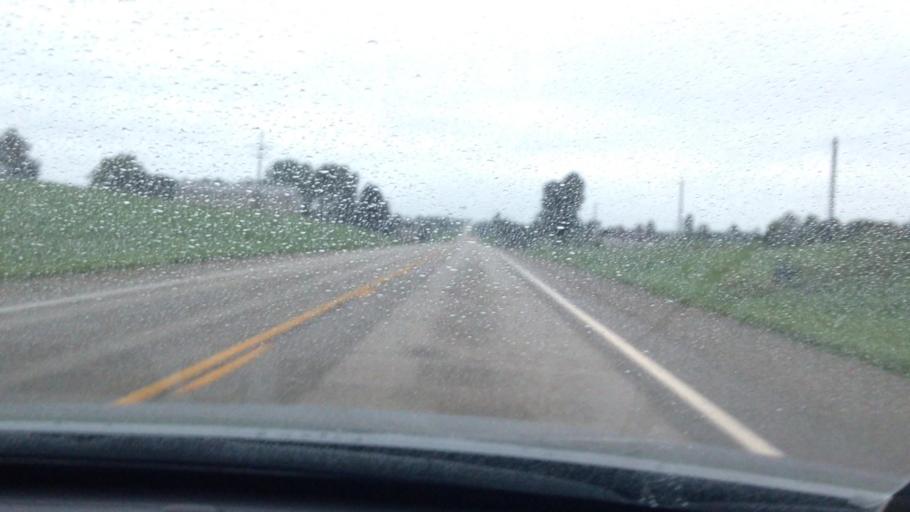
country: US
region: Kansas
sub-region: Brown County
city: Hiawatha
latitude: 39.8074
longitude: -95.5272
